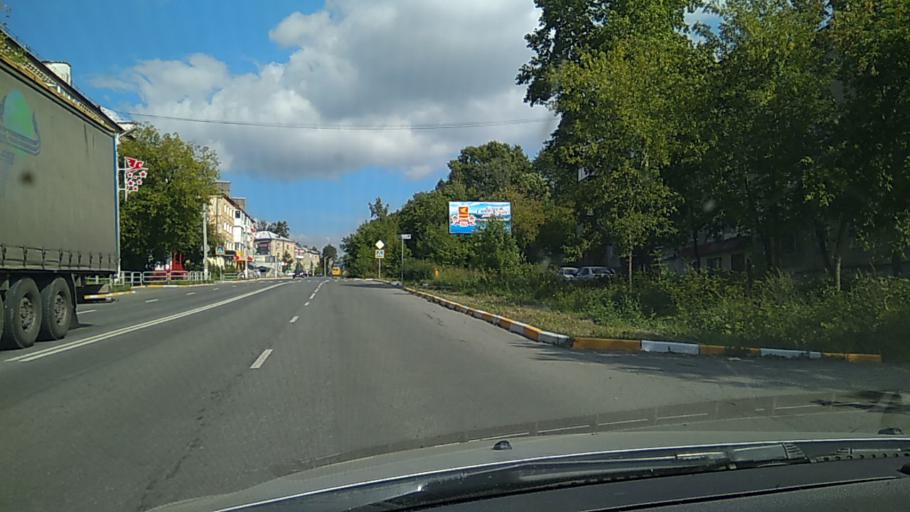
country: RU
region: Chelyabinsk
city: Zlatoust
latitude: 55.1141
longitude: 59.7166
